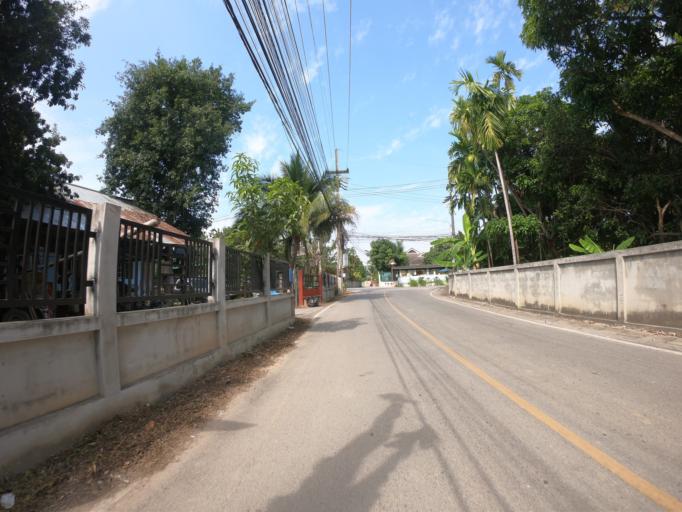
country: TH
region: Chiang Mai
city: San Sai
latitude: 18.8620
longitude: 99.0596
